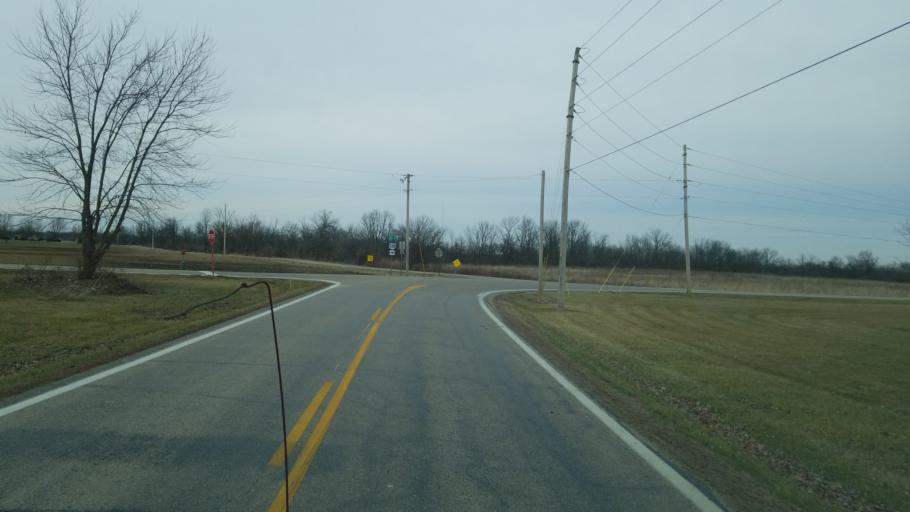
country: US
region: Ohio
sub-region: Pickaway County
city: Williamsport
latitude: 39.5484
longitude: -83.1214
